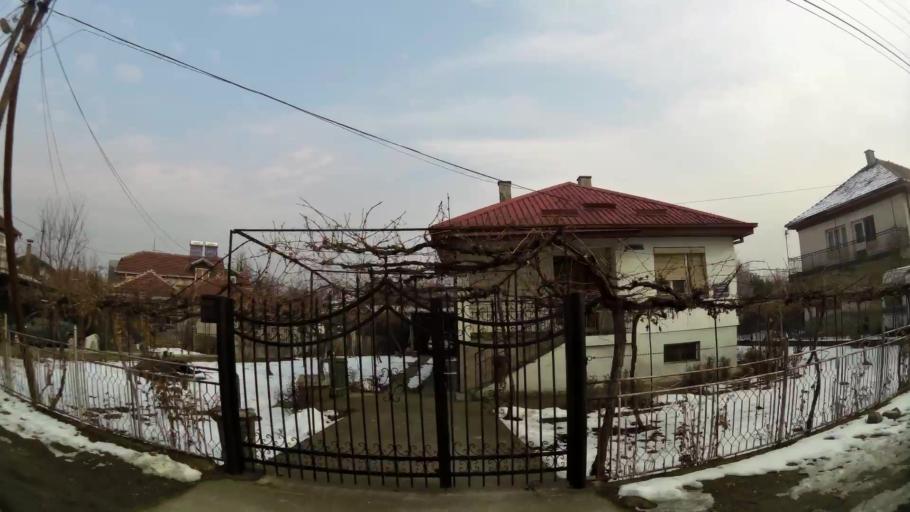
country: MK
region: Kisela Voda
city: Kisela Voda
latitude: 41.9971
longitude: 21.5027
